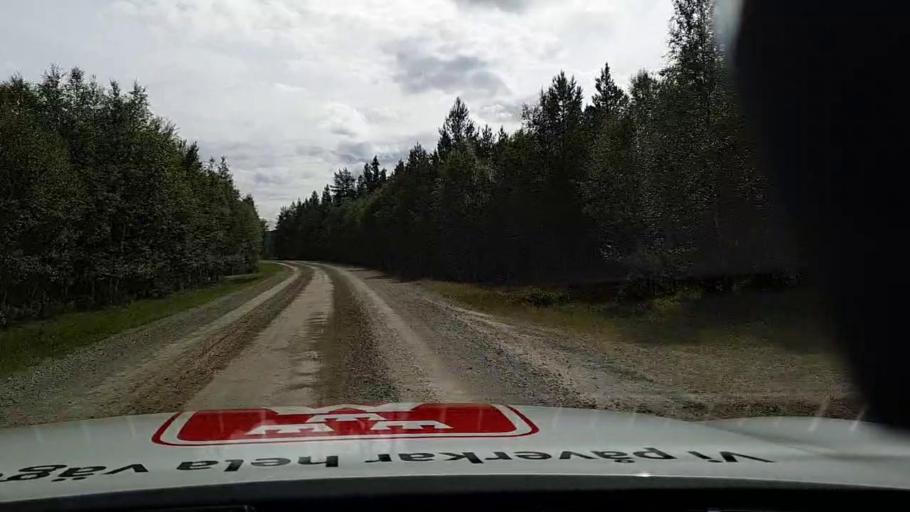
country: SE
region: Jaemtland
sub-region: Are Kommun
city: Jarpen
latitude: 62.5216
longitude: 13.4879
